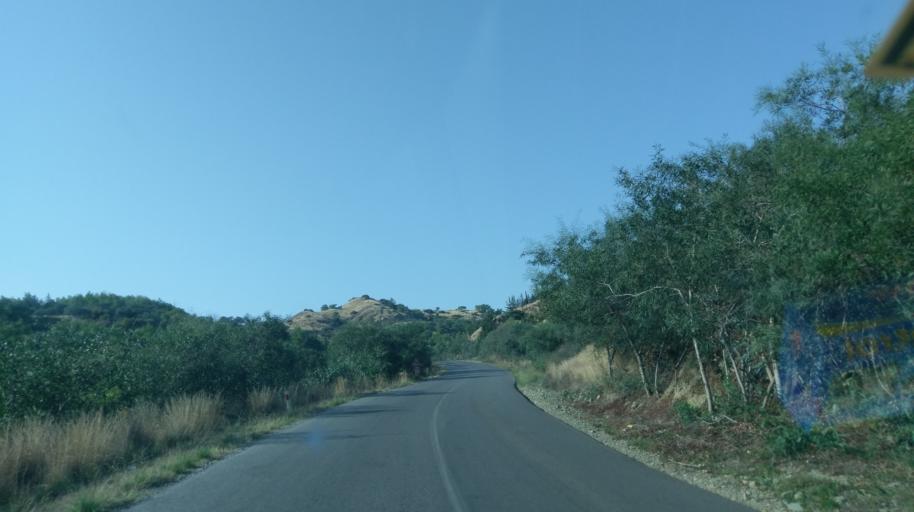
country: CY
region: Lefkosia
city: Kato Pyrgos
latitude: 35.1542
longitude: 32.7714
